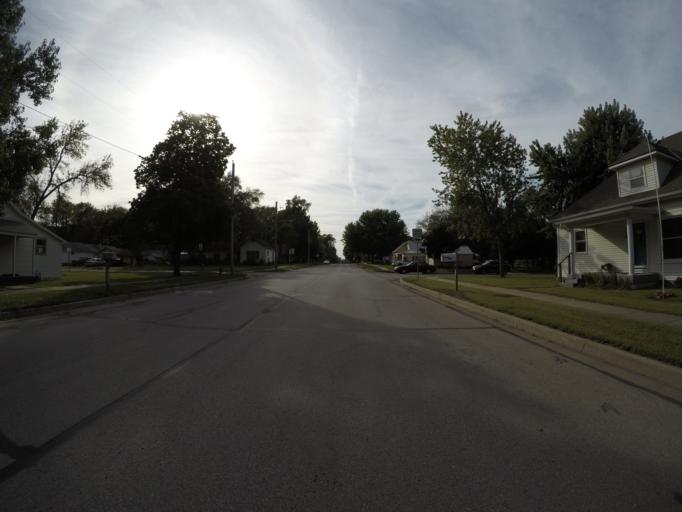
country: US
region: Kansas
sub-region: Johnson County
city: Edgerton
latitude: 38.7649
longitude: -95.0091
